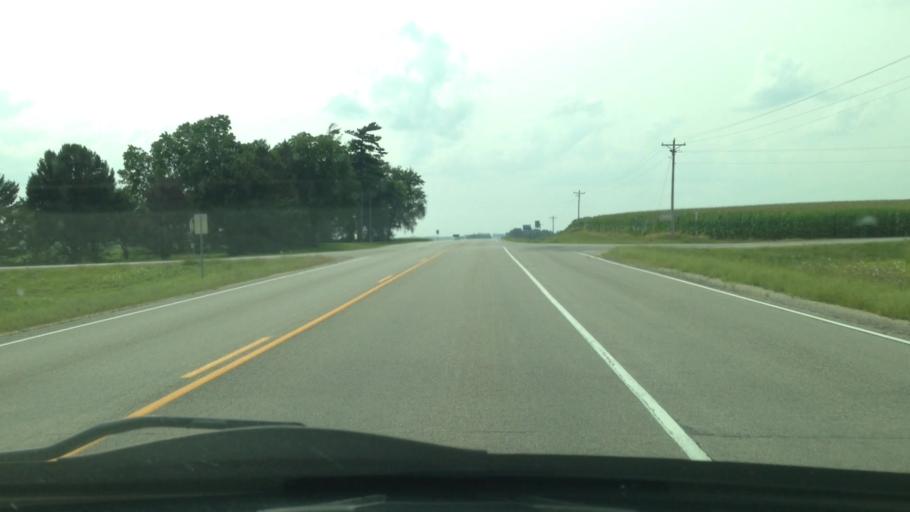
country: US
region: Minnesota
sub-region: Wabasha County
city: Elgin
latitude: 44.1654
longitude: -92.2588
